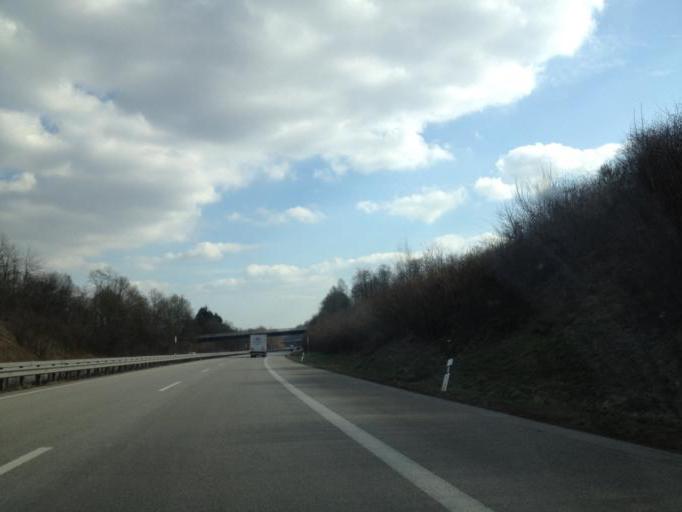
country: DE
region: Rheinland-Pfalz
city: Glan-Munchweiler
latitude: 49.4718
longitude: 7.4335
